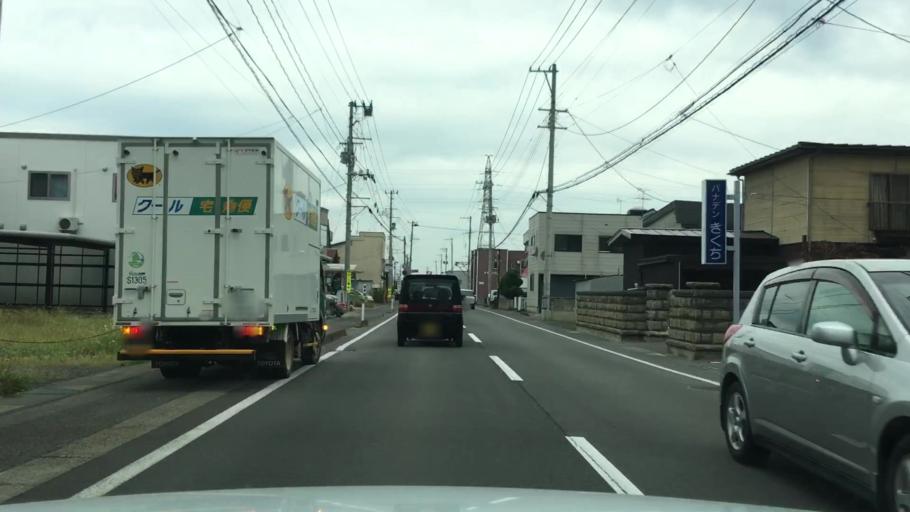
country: JP
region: Aomori
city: Hirosaki
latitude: 40.6247
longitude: 140.4562
